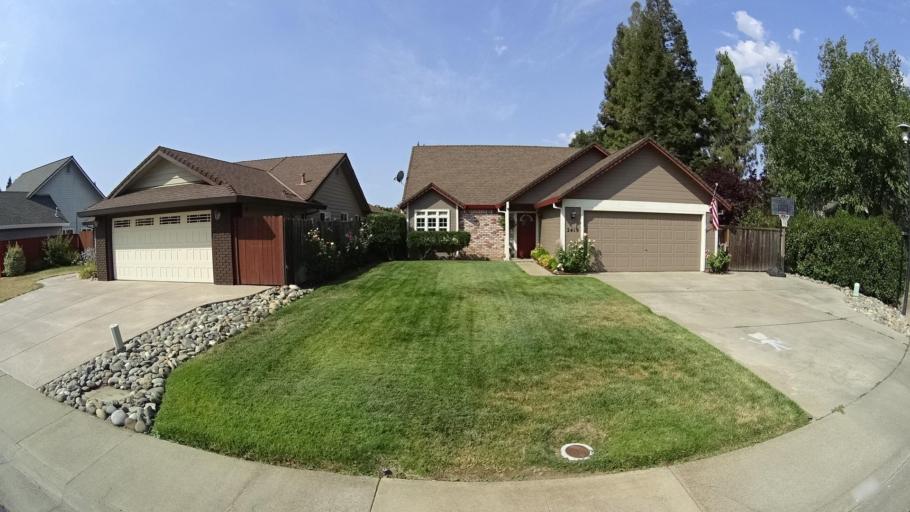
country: US
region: California
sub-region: Placer County
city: Rocklin
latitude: 38.7967
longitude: -121.2213
